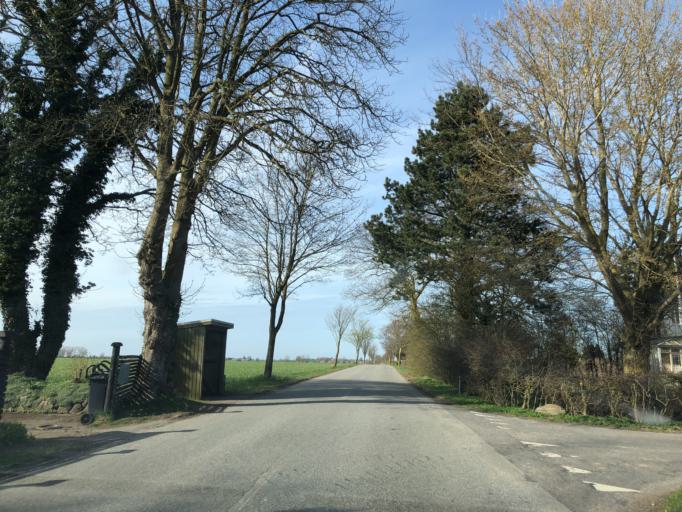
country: DK
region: Zealand
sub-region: Stevns Kommune
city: Store Heddinge
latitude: 55.3159
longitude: 12.4346
